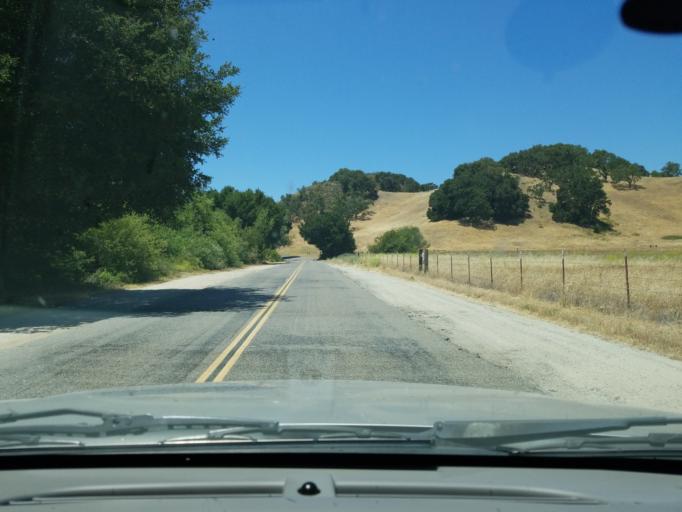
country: US
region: California
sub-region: Monterey County
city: Carmel Valley Village
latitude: 36.4429
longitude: -121.6484
